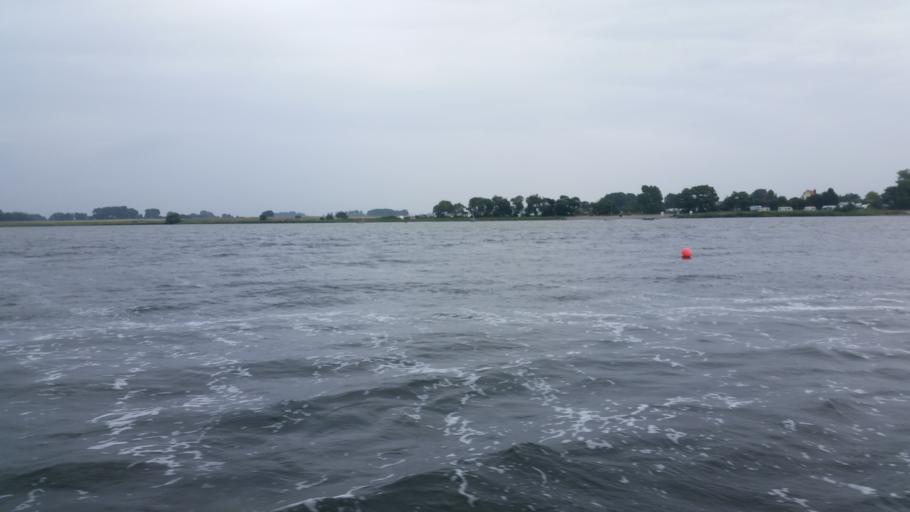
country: DE
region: Mecklenburg-Vorpommern
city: Hiddensee
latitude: 54.5172
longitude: 13.1579
